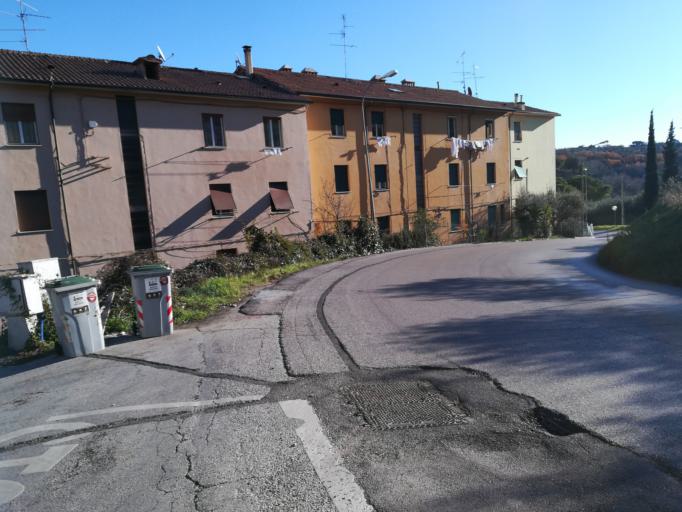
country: IT
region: Umbria
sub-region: Provincia di Perugia
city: Perugia
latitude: 43.0962
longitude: 12.3818
